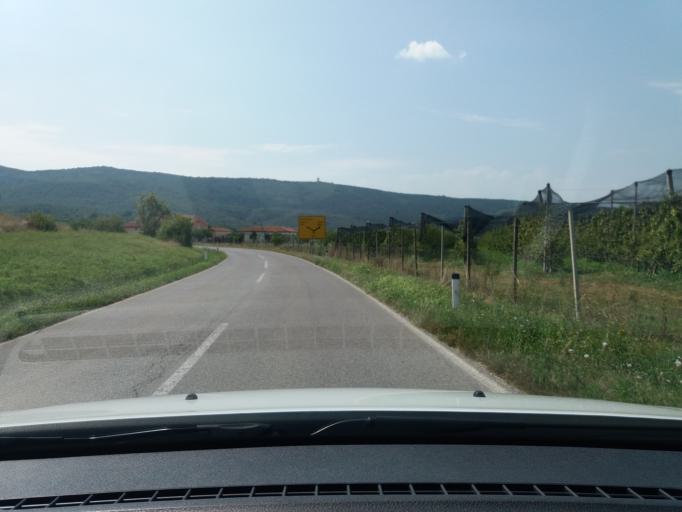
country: SI
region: Miren-Kostanjevica
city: Bilje
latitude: 45.8982
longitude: 13.6247
